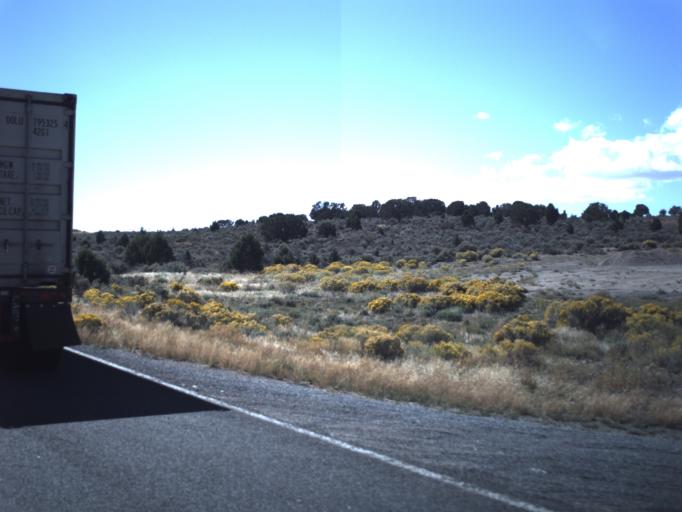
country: US
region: Utah
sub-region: Iron County
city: Parowan
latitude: 38.0778
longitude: -112.9576
